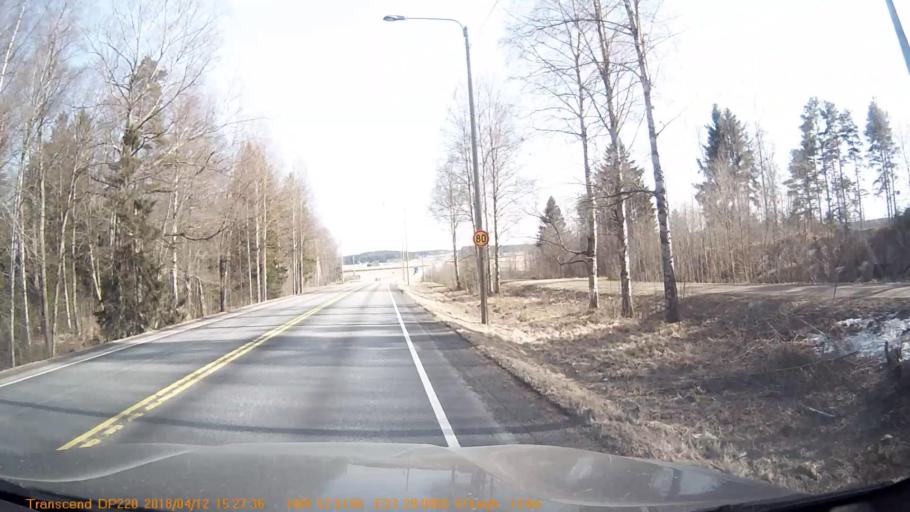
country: FI
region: Haeme
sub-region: Forssa
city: Jokioinen
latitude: 60.8766
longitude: 23.4856
